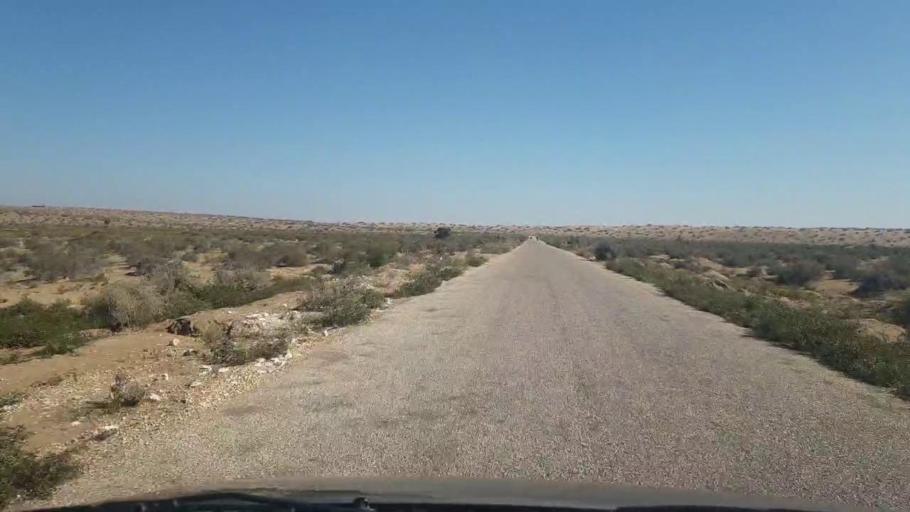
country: PK
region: Sindh
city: Bozdar
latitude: 27.0005
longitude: 68.8242
